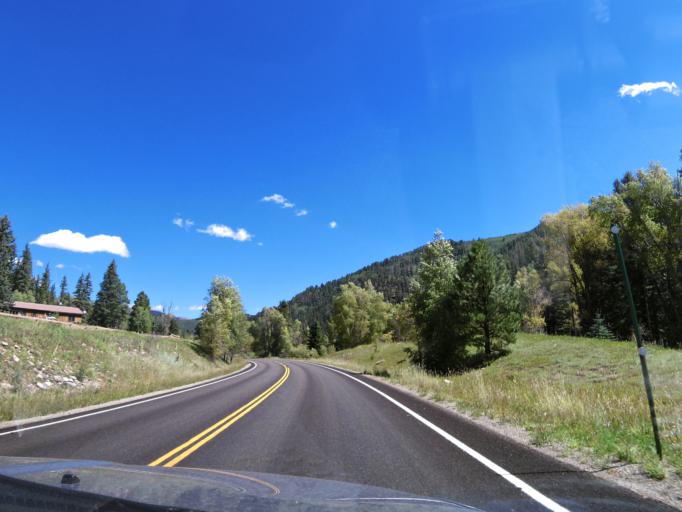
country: US
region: Colorado
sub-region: Montezuma County
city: Mancos
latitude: 37.6088
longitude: -108.0927
